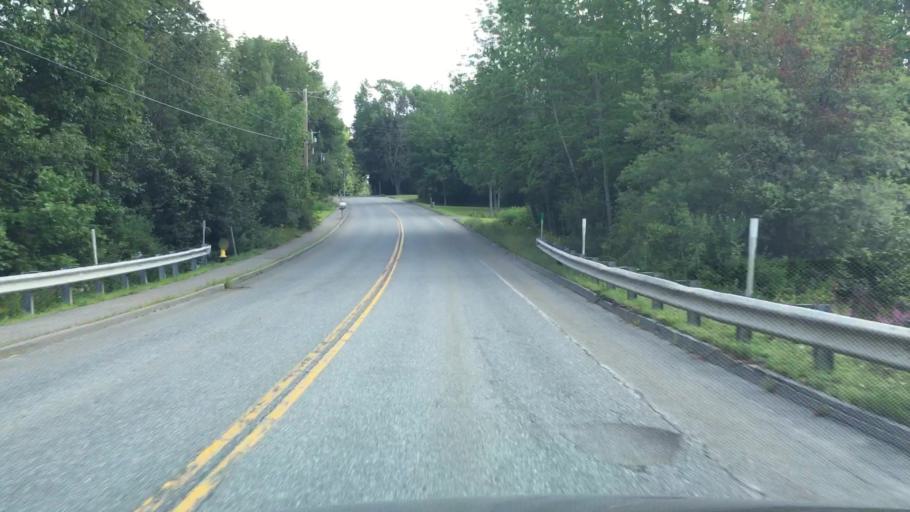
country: US
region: Maine
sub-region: Penobscot County
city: Hampden
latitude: 44.7363
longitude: -68.8603
